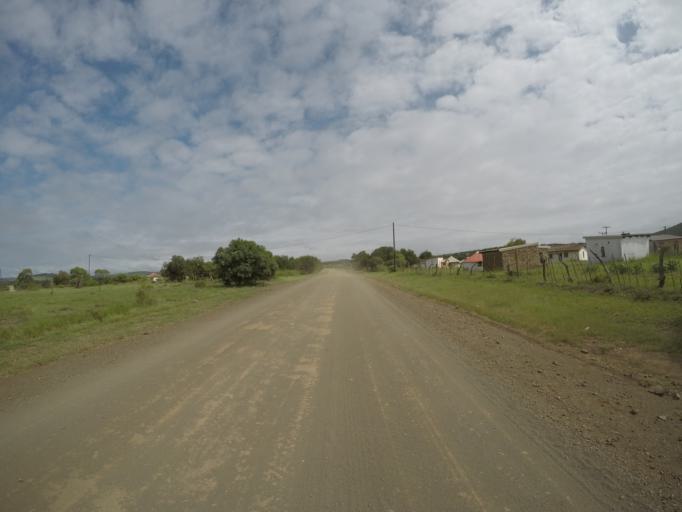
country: ZA
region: KwaZulu-Natal
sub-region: uThungulu District Municipality
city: Empangeni
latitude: -28.6164
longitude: 31.8501
